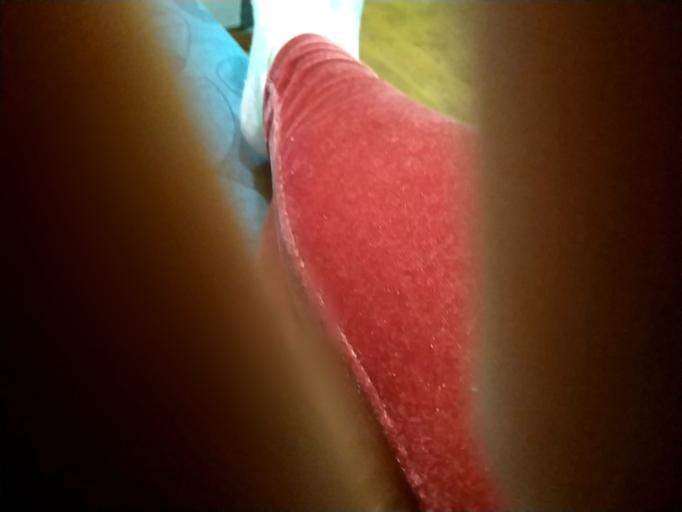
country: RU
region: Novgorod
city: Kulotino
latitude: 58.3899
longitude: 33.4701
